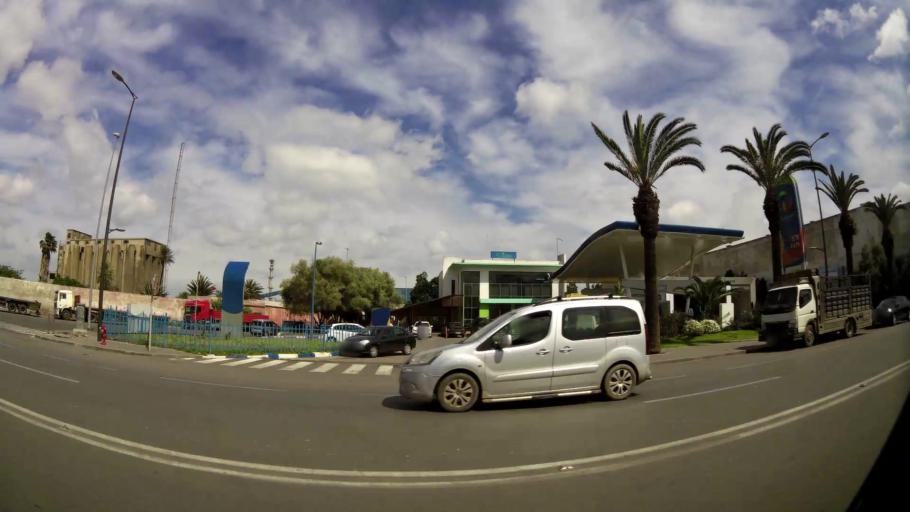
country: MA
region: Grand Casablanca
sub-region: Casablanca
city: Casablanca
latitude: 33.5993
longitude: -7.5701
